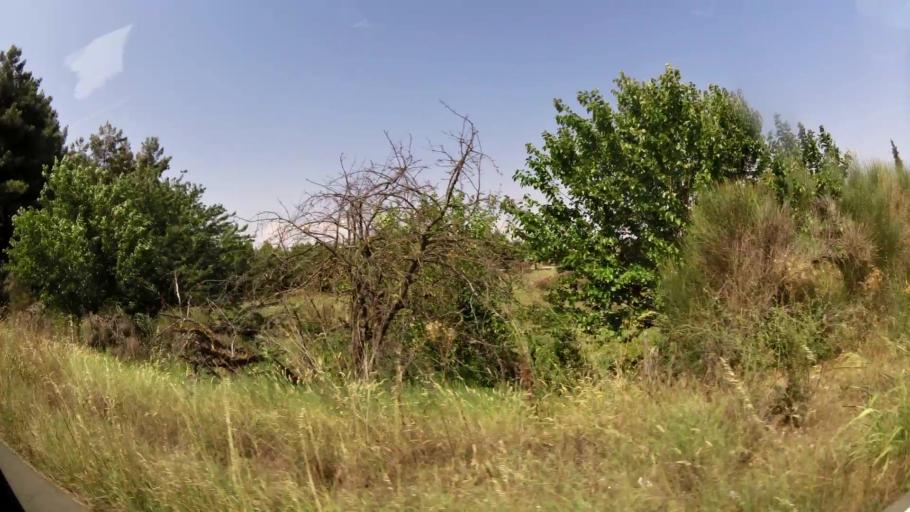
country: GR
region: Central Macedonia
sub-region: Nomos Thessalonikis
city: Agios Athanasios
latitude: 40.7210
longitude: 22.7140
